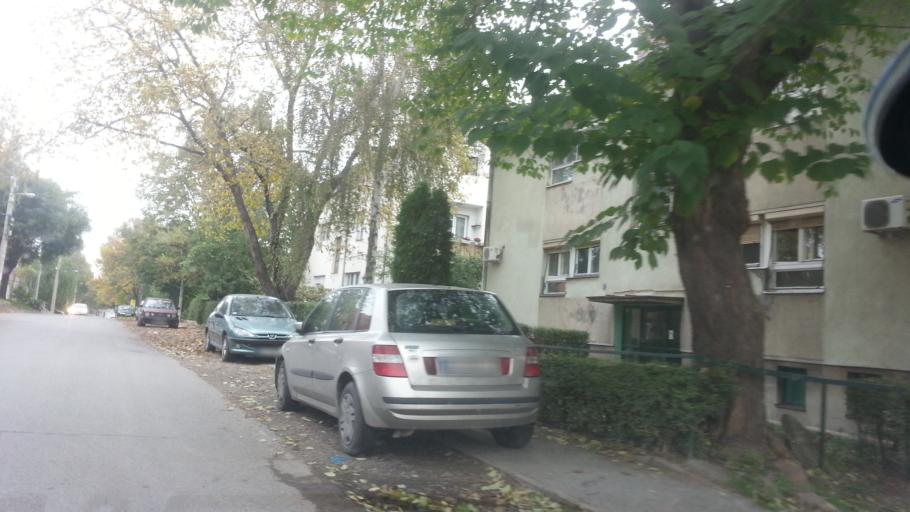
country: RS
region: Central Serbia
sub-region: Belgrade
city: Zemun
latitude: 44.8381
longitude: 20.3964
